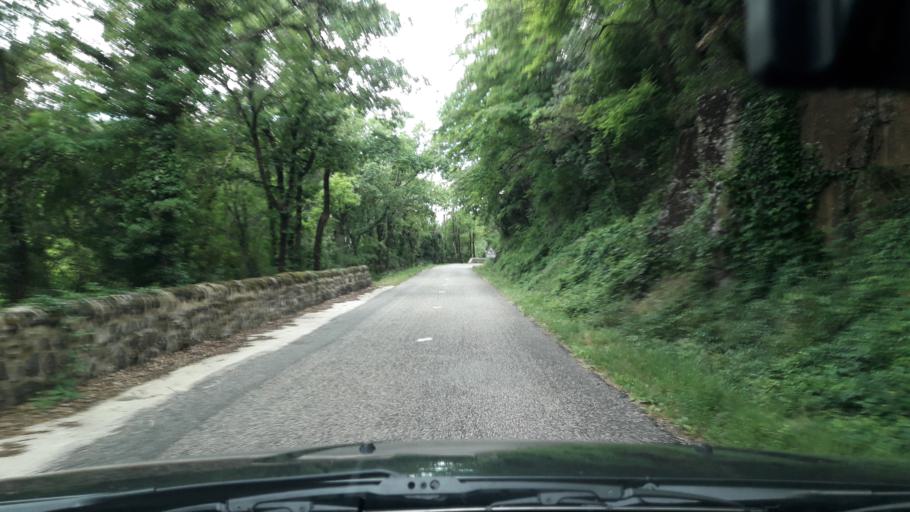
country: FR
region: Rhone-Alpes
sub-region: Departement de l'Ardeche
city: Saint-Priest
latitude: 44.6520
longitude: 4.5194
